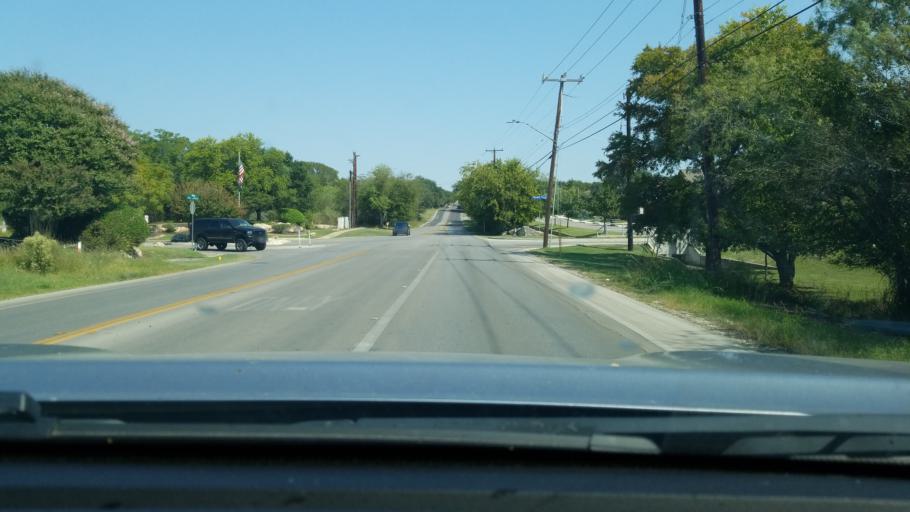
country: US
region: Texas
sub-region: Bexar County
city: Leon Valley
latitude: 29.5447
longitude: -98.6054
